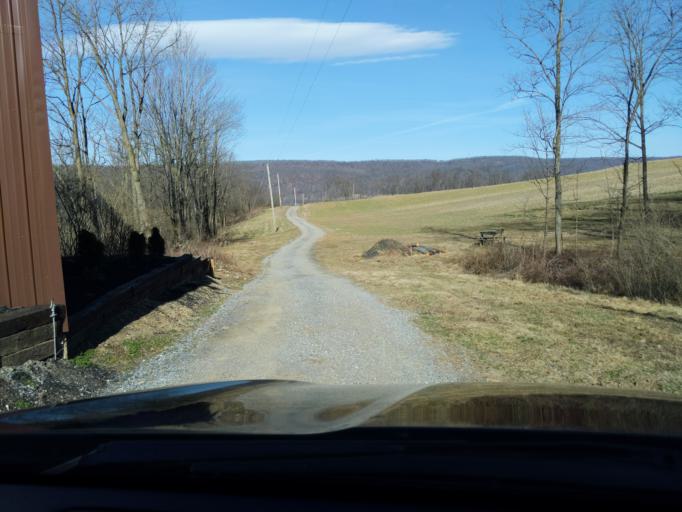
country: US
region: Pennsylvania
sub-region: Blair County
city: Martinsburg
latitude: 40.3894
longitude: -78.2673
